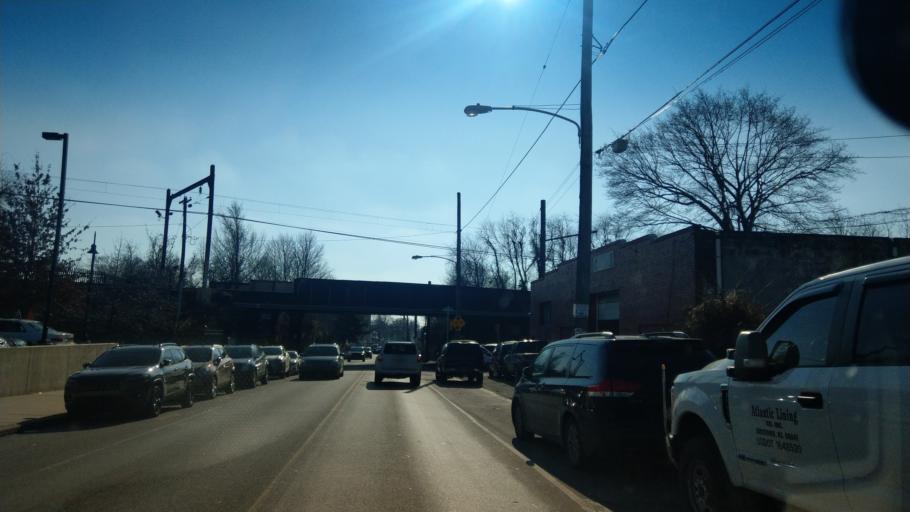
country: US
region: Pennsylvania
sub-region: Montgomery County
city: Rockledge
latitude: 40.0332
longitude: -75.1241
